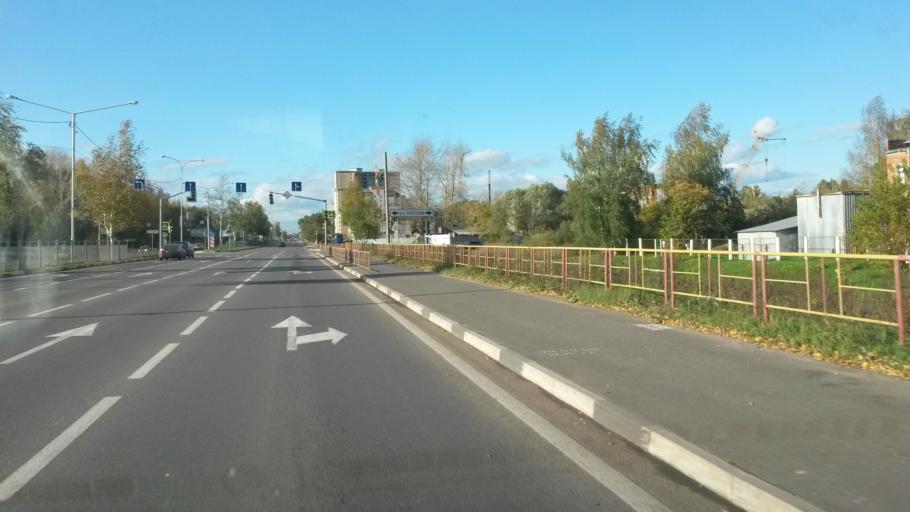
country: RU
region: Jaroslavl
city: Yaroslavl
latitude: 57.5604
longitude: 39.9362
